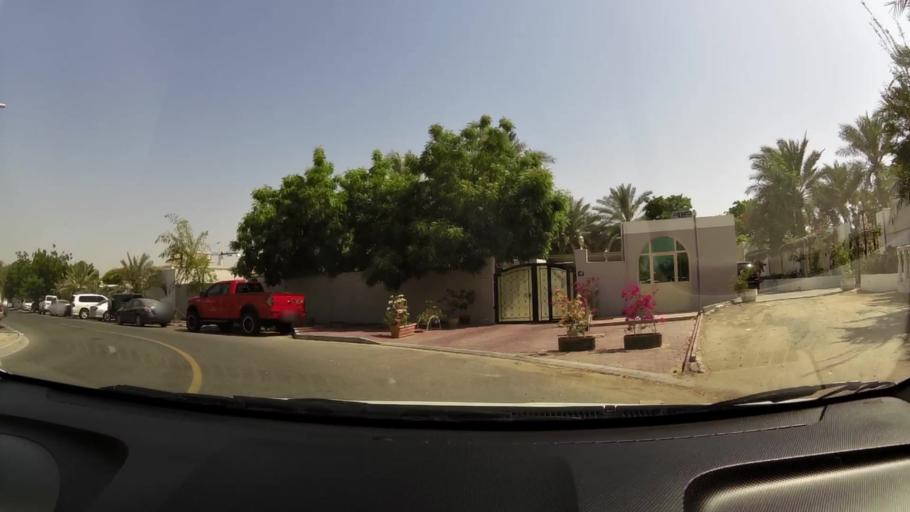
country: AE
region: Ash Shariqah
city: Sharjah
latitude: 25.2683
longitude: 55.3649
